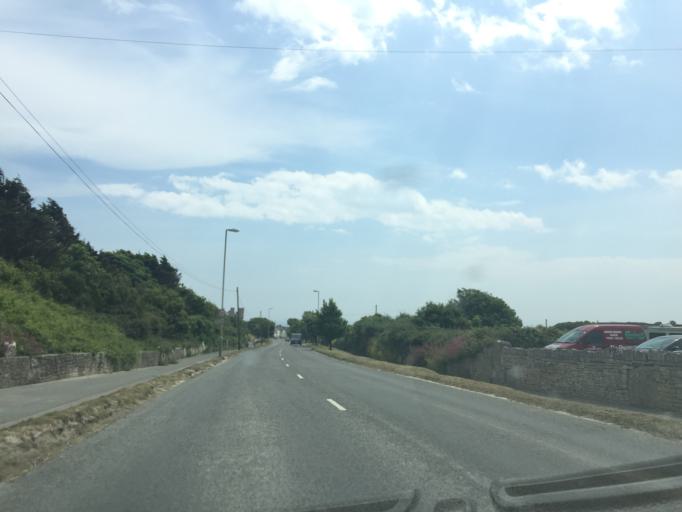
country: GB
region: England
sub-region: Dorset
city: Fortuneswell
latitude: 50.5521
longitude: -2.4374
